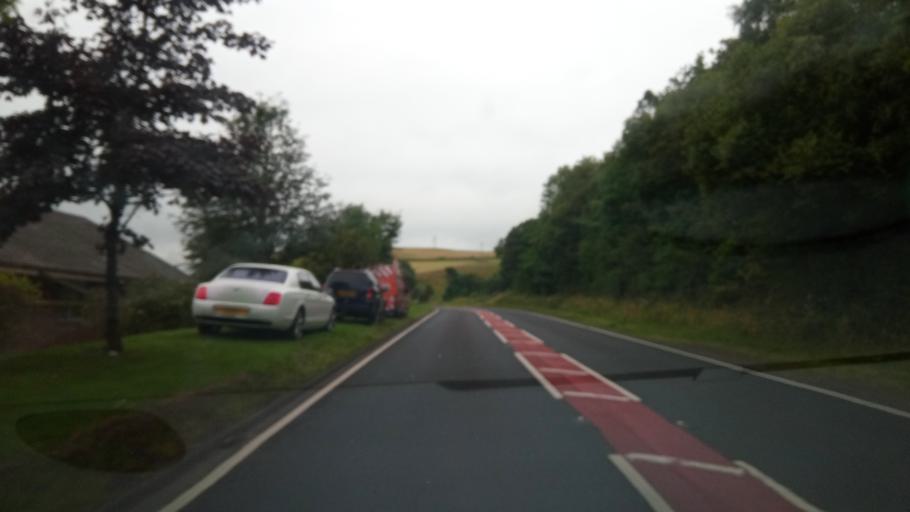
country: GB
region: Scotland
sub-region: The Scottish Borders
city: Hawick
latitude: 55.3843
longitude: -2.8672
